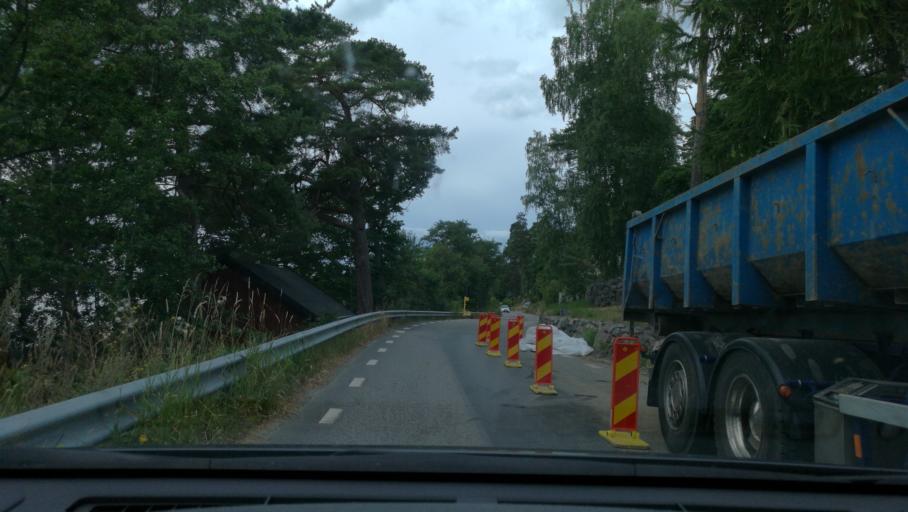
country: SE
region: OEstergoetland
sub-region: Norrkopings Kommun
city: Krokek
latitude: 58.6639
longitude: 16.3634
